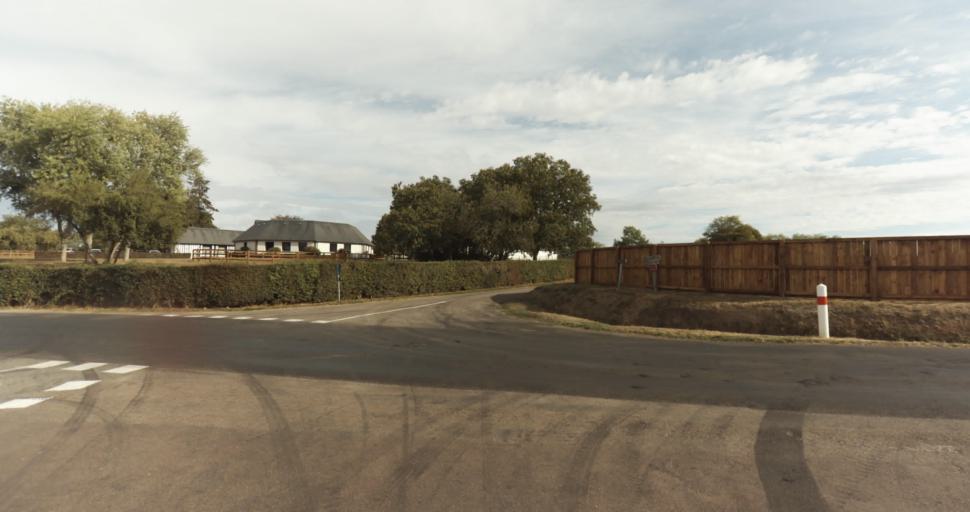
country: FR
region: Lower Normandy
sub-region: Departement de l'Orne
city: Vimoutiers
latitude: 48.9321
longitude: 0.2381
